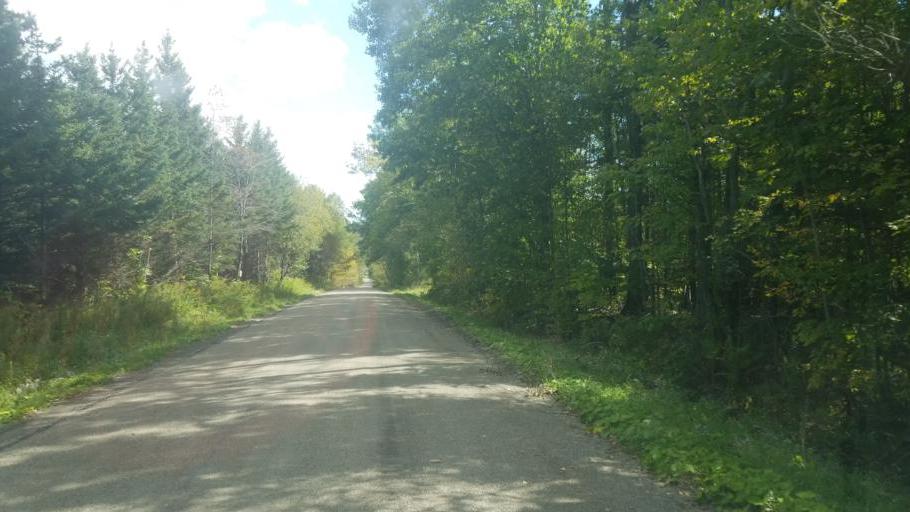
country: US
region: New York
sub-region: Allegany County
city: Cuba
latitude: 42.1929
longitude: -78.3145
